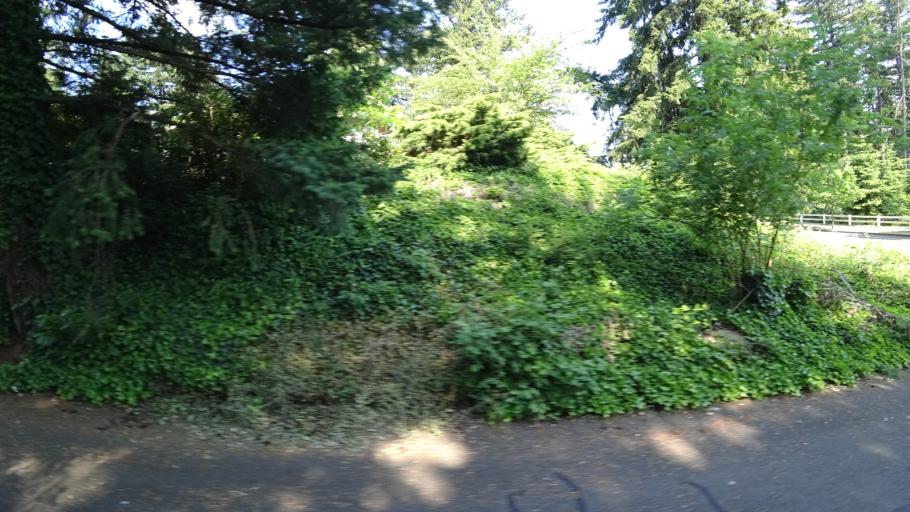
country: US
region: Oregon
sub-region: Clackamas County
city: Happy Valley
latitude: 45.4399
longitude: -122.5443
